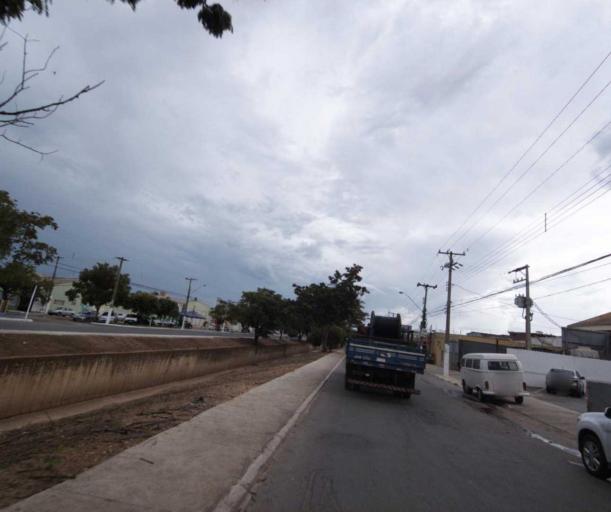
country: BR
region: Mato Grosso
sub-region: Cuiaba
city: Cuiaba
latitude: -15.6159
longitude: -56.0759
